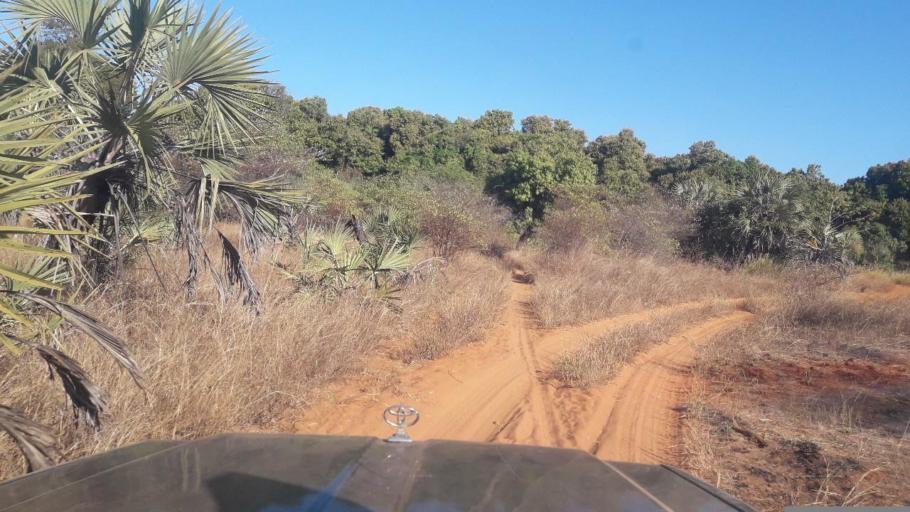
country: MG
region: Boeny
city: Sitampiky
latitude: -16.4052
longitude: 45.5989
